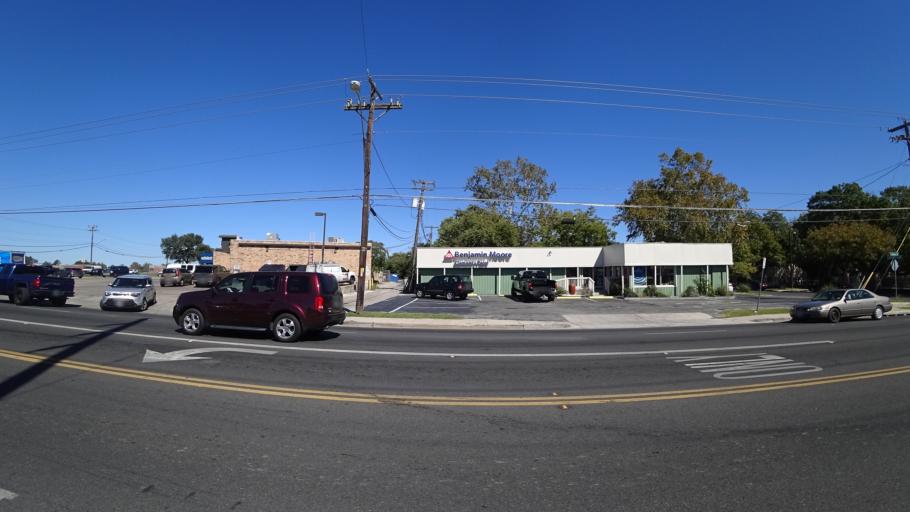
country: US
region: Texas
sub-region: Travis County
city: Austin
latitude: 30.3345
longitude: -97.7394
